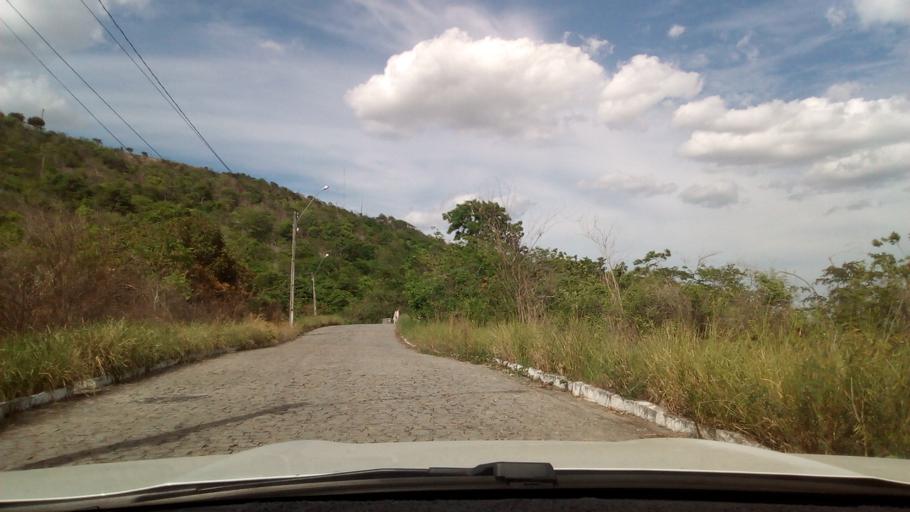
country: BR
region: Paraiba
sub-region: Guarabira
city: Guarabira
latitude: -6.8341
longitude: -35.4957
